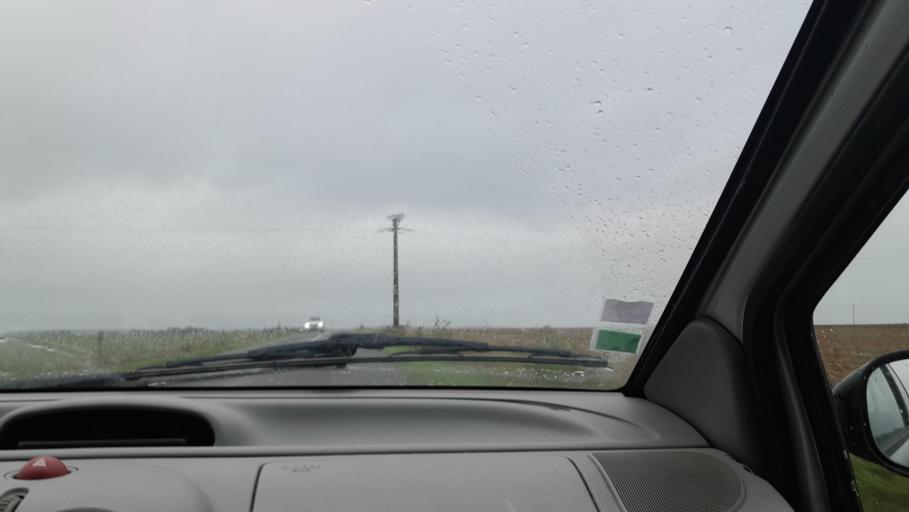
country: FR
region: Pays de la Loire
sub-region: Departement de la Mayenne
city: Congrier
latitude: 47.8565
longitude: -1.1331
